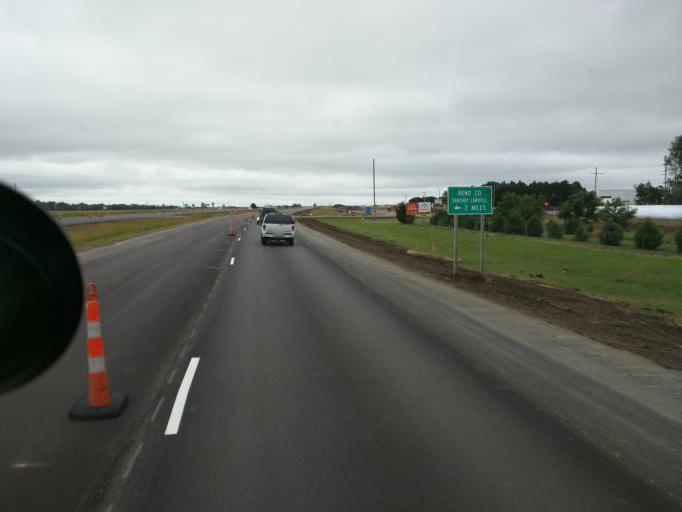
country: US
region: Kansas
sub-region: Reno County
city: South Hutchinson
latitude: 38.0141
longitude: -97.9967
